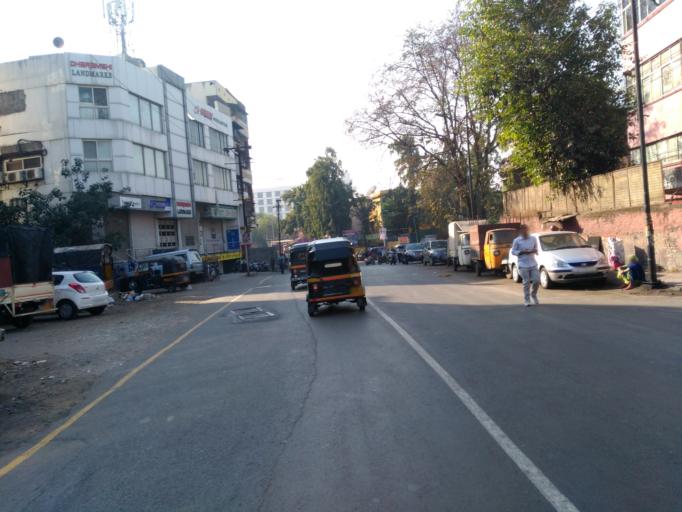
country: IN
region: Maharashtra
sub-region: Pune Division
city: Pune
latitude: 18.5079
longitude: 73.8723
